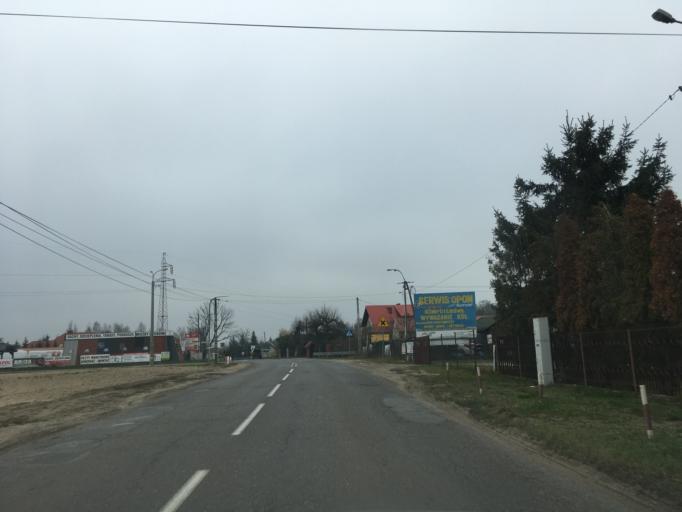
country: PL
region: Masovian Voivodeship
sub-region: Powiat piaseczynski
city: Lesznowola
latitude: 52.0754
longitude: 20.9663
